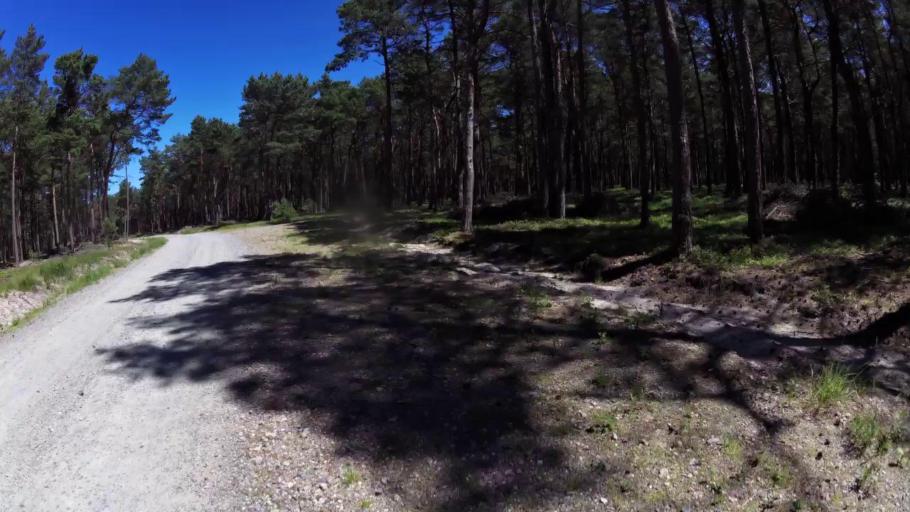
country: PL
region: West Pomeranian Voivodeship
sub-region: Powiat gryficki
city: Trzebiatow
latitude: 54.1099
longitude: 15.1963
